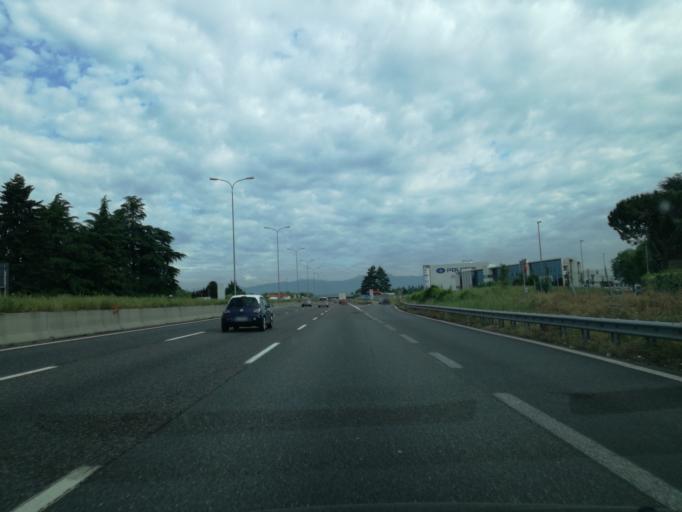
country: IT
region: Lombardy
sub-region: Provincia di Monza e Brianza
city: Carate Brianza
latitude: 45.6584
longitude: 9.2254
